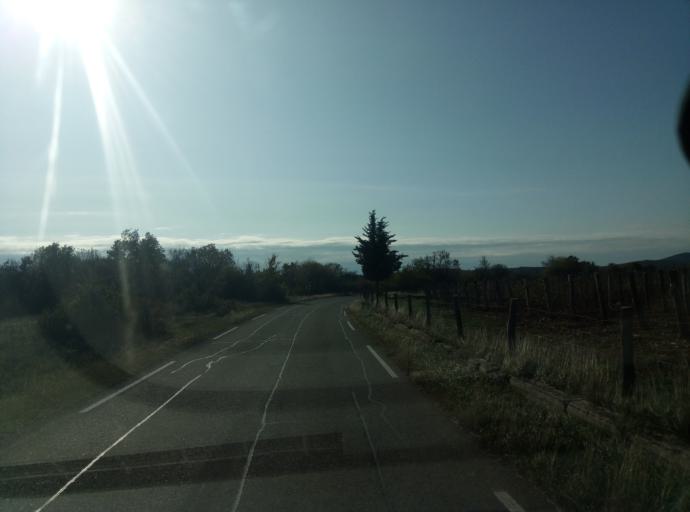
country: SI
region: Komen
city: Komen
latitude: 45.8071
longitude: 13.7240
